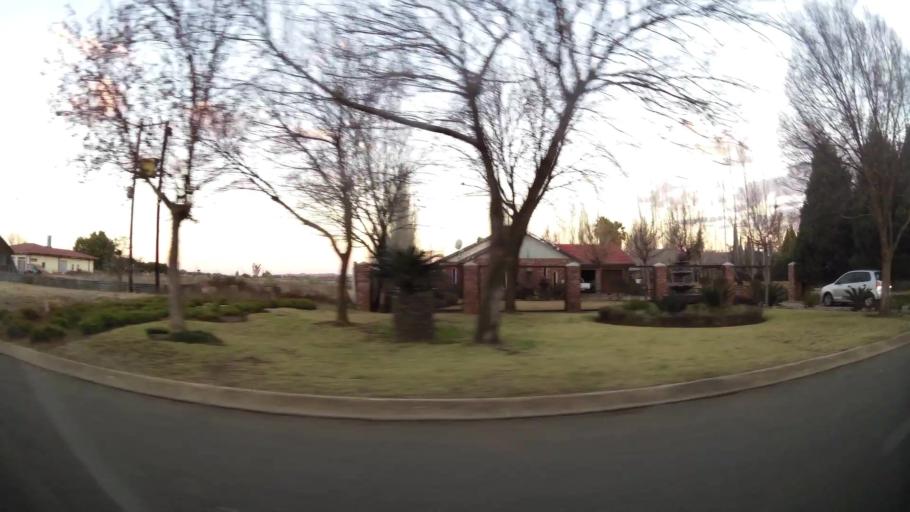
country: ZA
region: North-West
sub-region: Dr Kenneth Kaunda District Municipality
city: Potchefstroom
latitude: -26.7199
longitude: 27.1231
